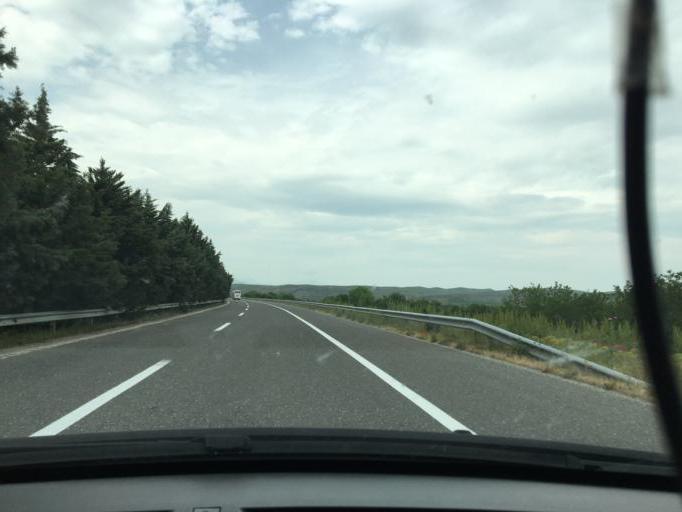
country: MK
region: Gradsko
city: Gradsko
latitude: 41.5567
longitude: 22.0185
